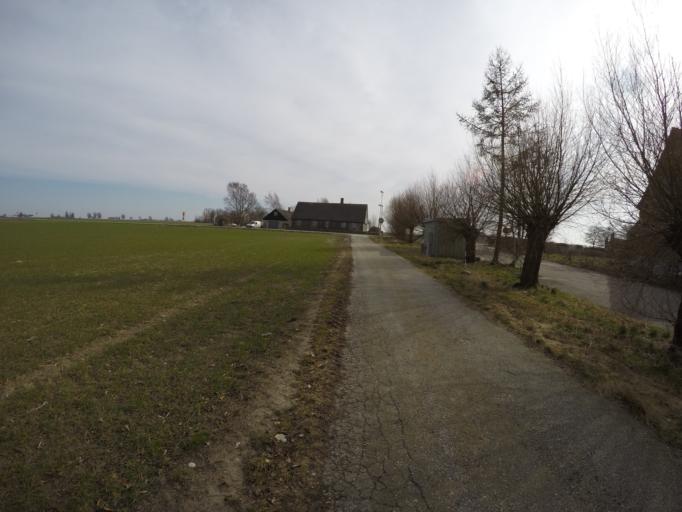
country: SE
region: Skane
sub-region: Ystads Kommun
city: Kopingebro
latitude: 55.4294
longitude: 14.1147
